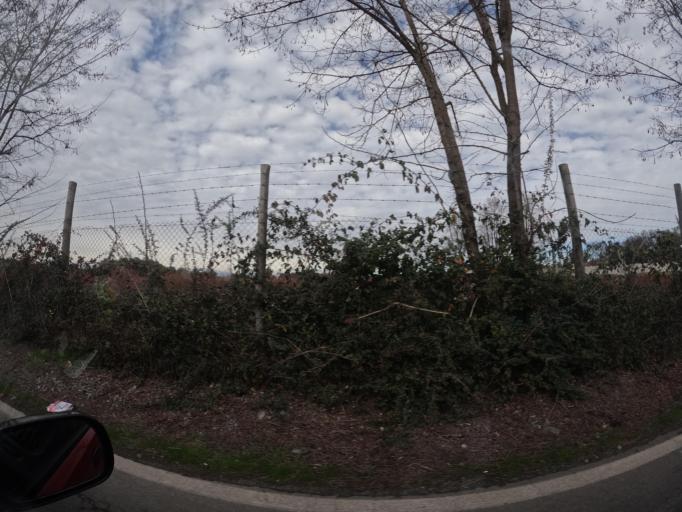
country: CL
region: Maule
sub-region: Provincia de Linares
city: Linares
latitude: -35.8655
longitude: -71.6224
